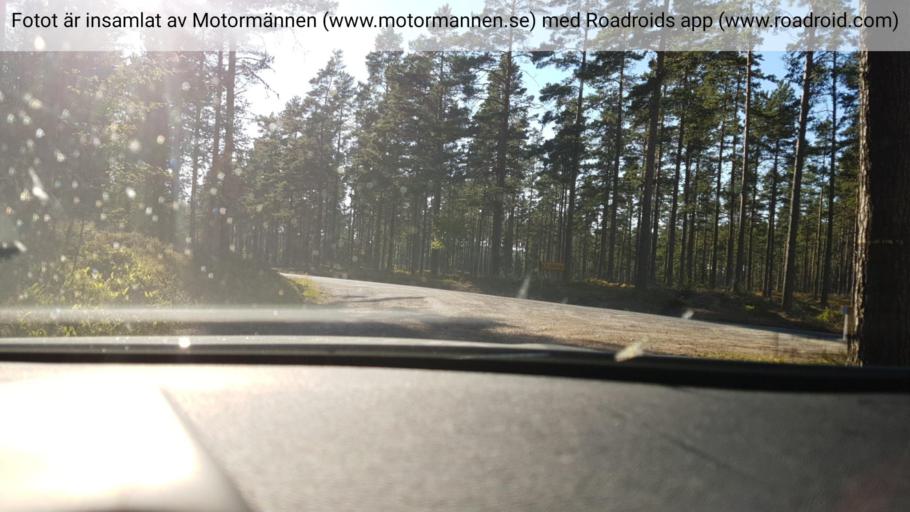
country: SE
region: Vaestra Goetaland
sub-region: Tidaholms Kommun
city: Tidaholm
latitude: 58.0996
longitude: 14.0950
